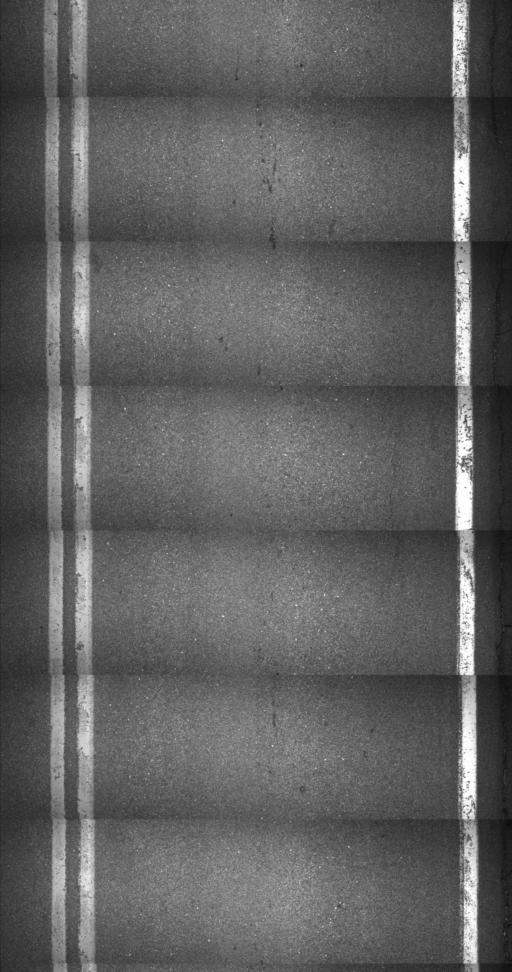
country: US
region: Vermont
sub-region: Rutland County
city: Brandon
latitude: 43.7760
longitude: -73.2033
